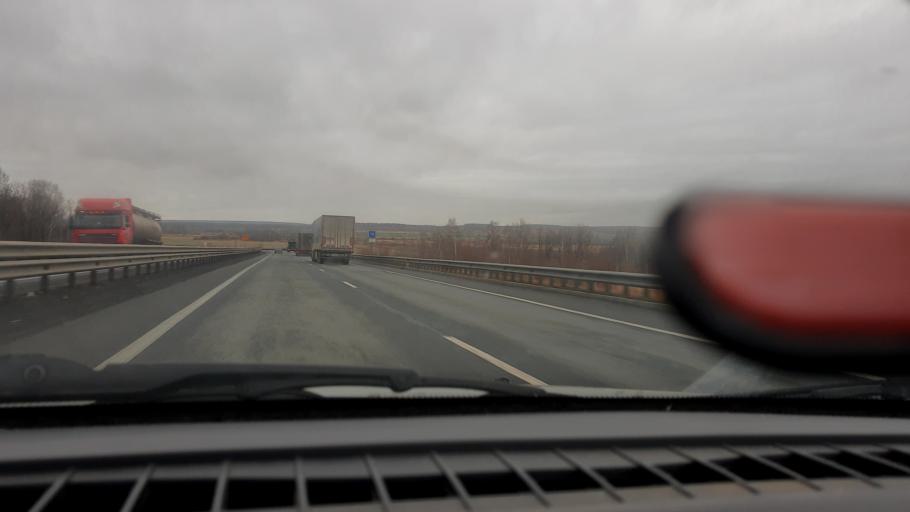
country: RU
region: Nizjnij Novgorod
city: Burevestnik
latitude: 56.1293
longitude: 43.7830
